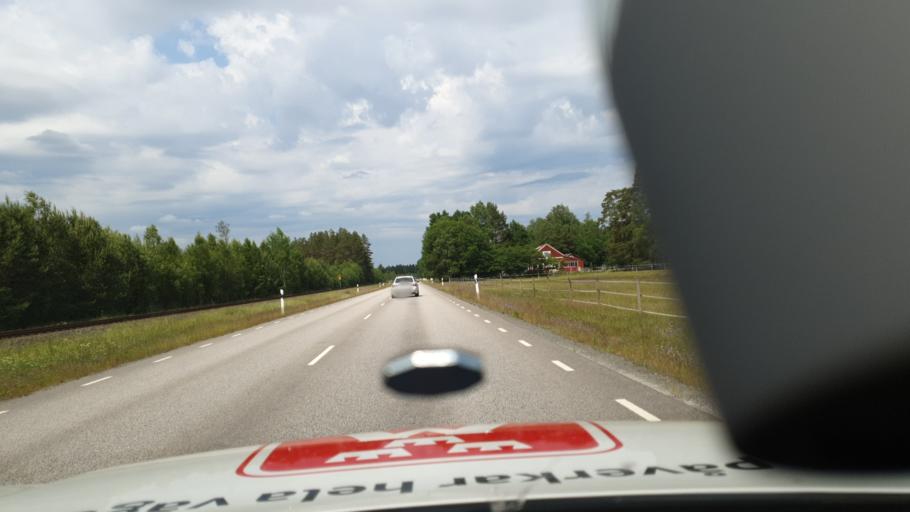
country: SE
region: Joenkoeping
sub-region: Varnamo Kommun
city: Varnamo
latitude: 57.2422
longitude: 14.0446
